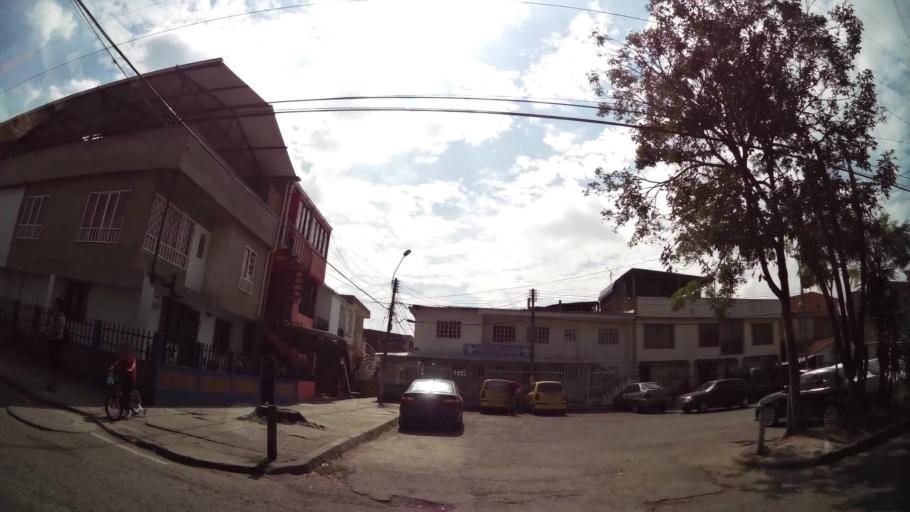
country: CO
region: Valle del Cauca
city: Cali
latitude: 3.4961
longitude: -76.4900
